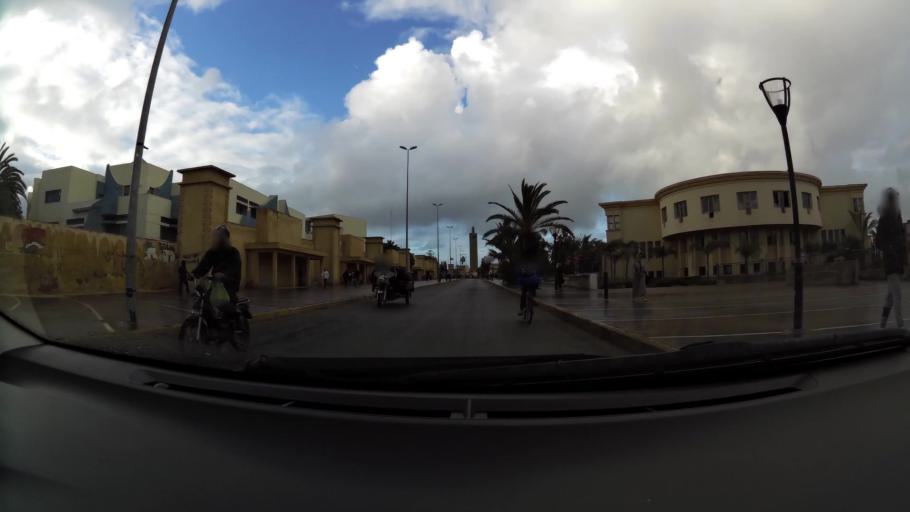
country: MA
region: Grand Casablanca
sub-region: Mohammedia
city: Mohammedia
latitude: 33.6842
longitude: -7.3905
